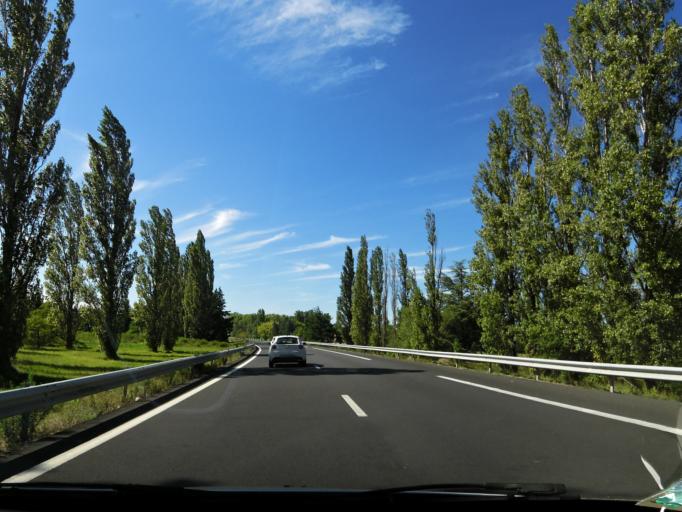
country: FR
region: Provence-Alpes-Cote d'Azur
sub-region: Departement du Vaucluse
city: Orange
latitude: 44.1313
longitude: 4.7910
